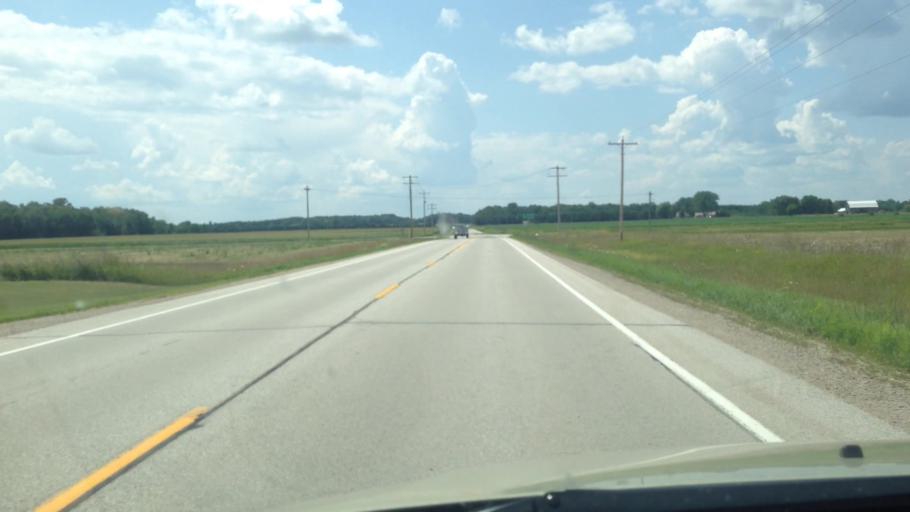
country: US
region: Wisconsin
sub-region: Brown County
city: Pulaski
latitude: 44.6461
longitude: -88.1578
